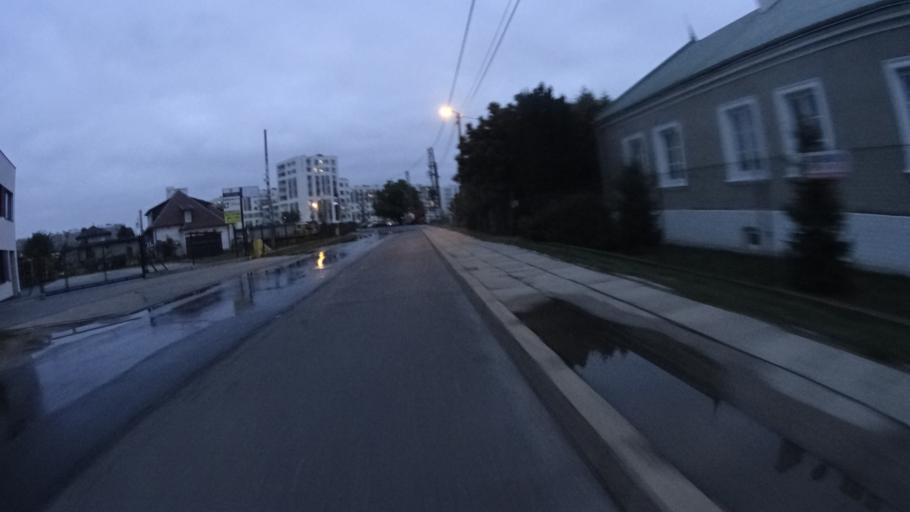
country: PL
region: Masovian Voivodeship
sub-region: Warszawa
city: Ursus
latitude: 52.2264
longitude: 20.8907
